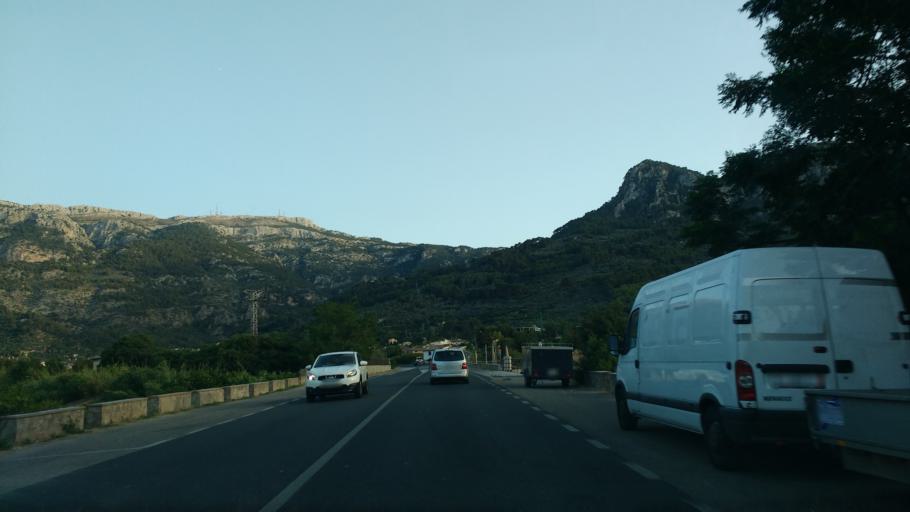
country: ES
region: Balearic Islands
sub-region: Illes Balears
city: Soller
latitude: 39.7752
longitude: 2.7056
